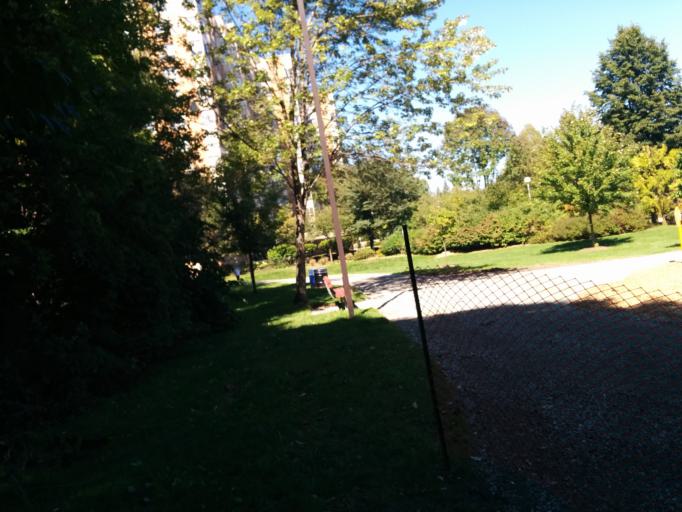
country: CA
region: Ontario
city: Etobicoke
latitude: 43.5872
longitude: -79.5494
